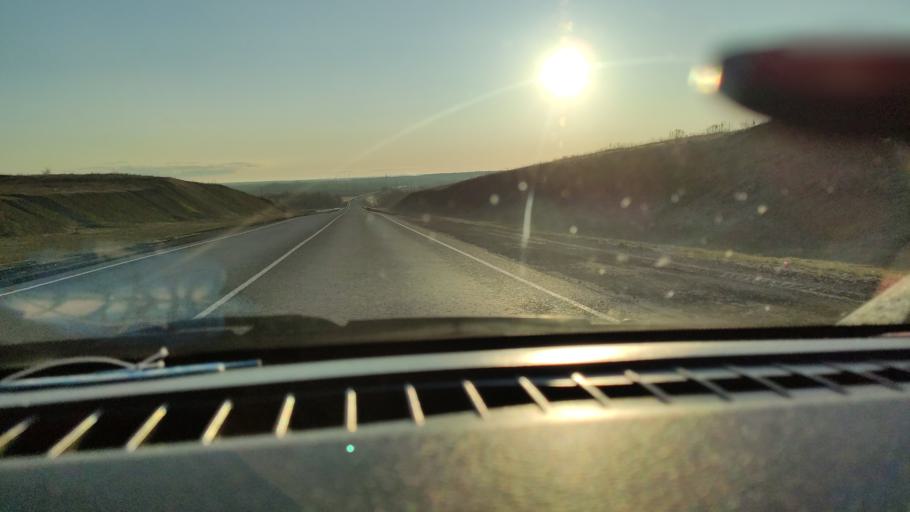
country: RU
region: Saratov
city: Sennoy
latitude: 52.1383
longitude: 46.8800
